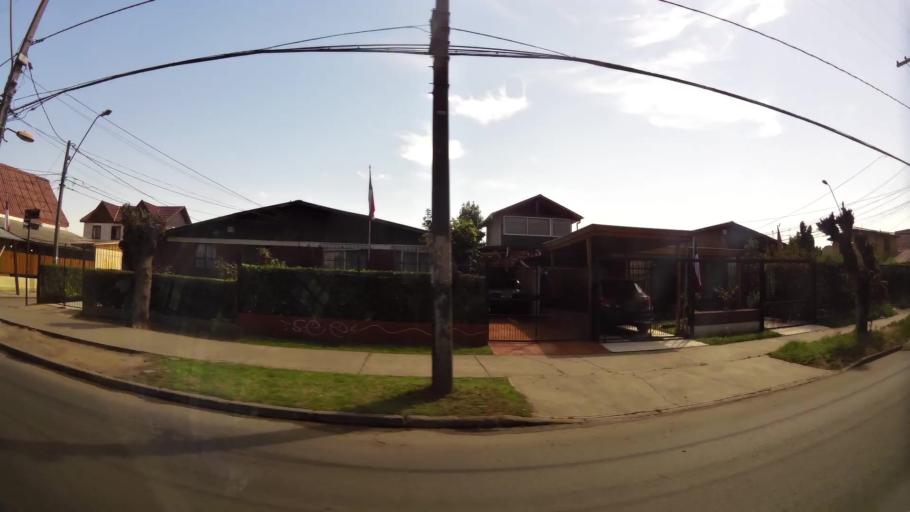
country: CL
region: Santiago Metropolitan
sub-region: Provincia de Santiago
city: Lo Prado
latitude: -33.4772
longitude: -70.7279
